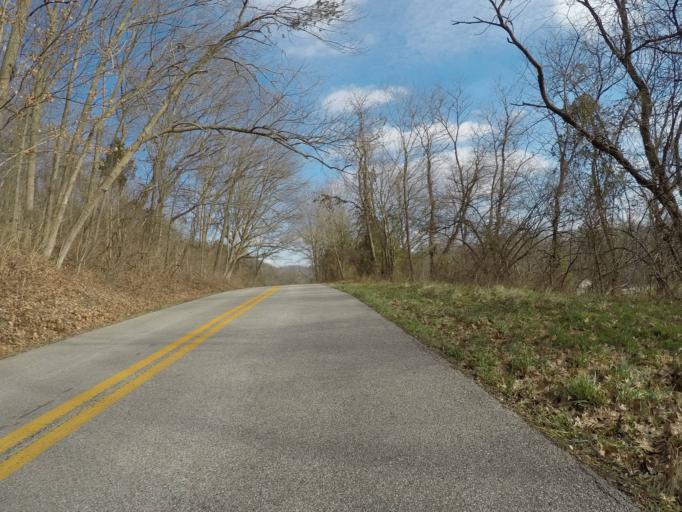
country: US
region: West Virginia
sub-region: Cabell County
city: Pea Ridge
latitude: 38.4273
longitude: -82.3247
